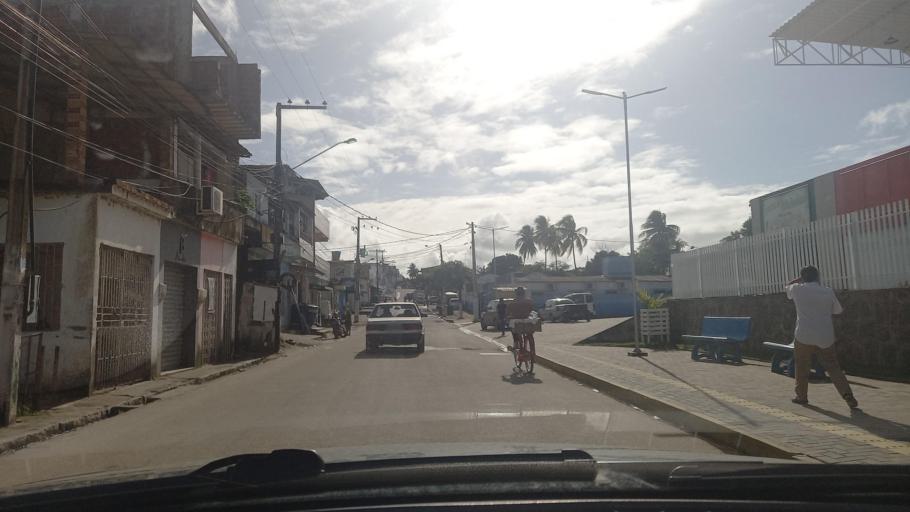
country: BR
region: Pernambuco
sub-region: Vitoria De Santo Antao
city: Vitoria de Santo Antao
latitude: -8.1010
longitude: -35.2819
